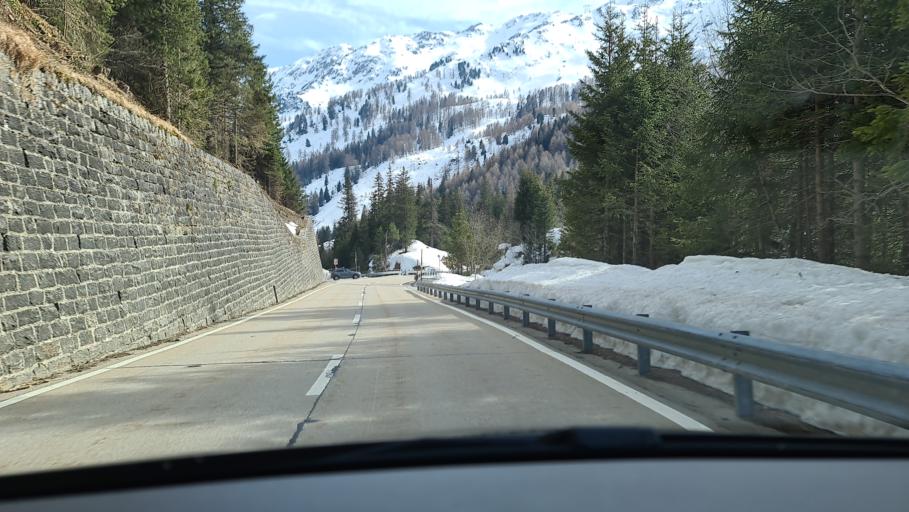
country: CH
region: Ticino
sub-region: Leventina District
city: Faido
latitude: 46.5290
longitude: 8.8495
